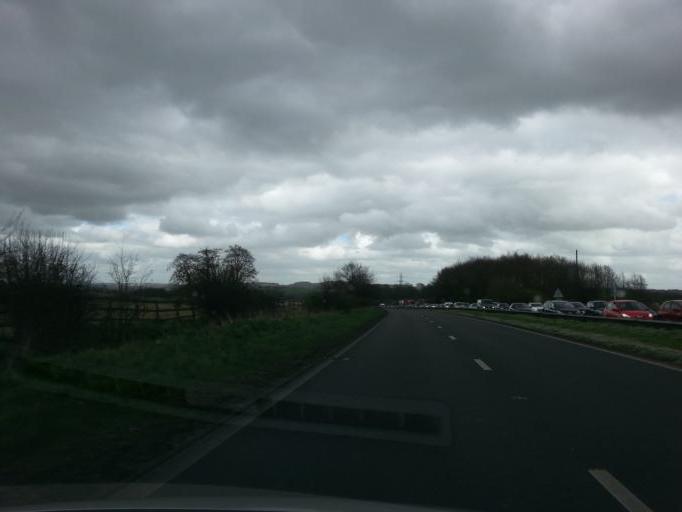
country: GB
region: England
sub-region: Wiltshire
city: Amesbury
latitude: 51.1771
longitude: -1.8063
